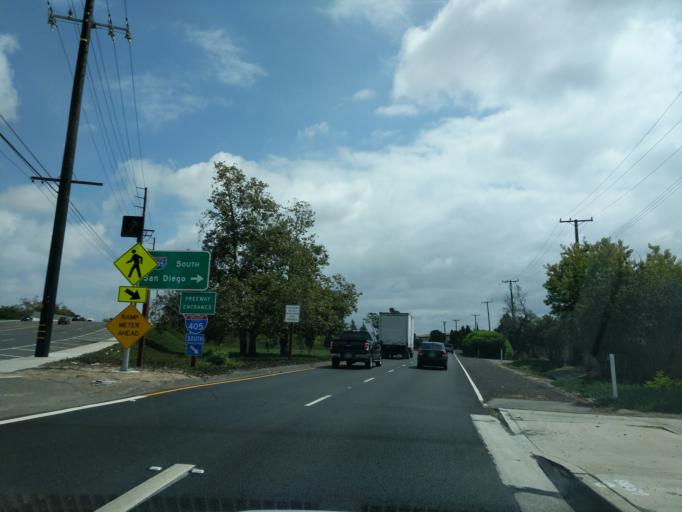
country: US
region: California
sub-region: Orange County
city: Fountain Valley
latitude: 33.7157
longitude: -117.9699
